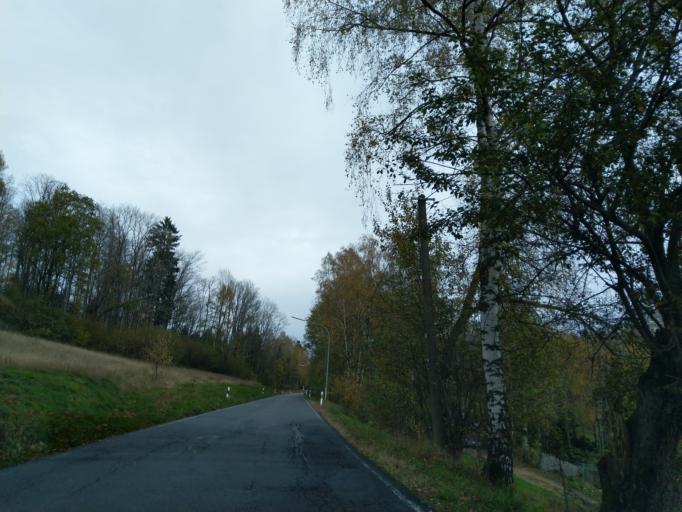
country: DE
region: Bavaria
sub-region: Lower Bavaria
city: Schofweg
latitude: 48.8165
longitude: 13.2350
